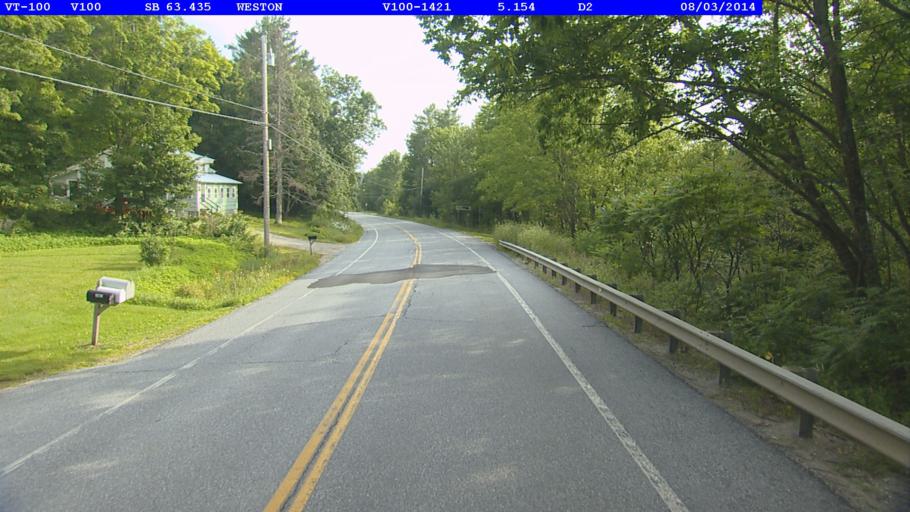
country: US
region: Vermont
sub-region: Windsor County
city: Chester
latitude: 43.3184
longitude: -72.7865
